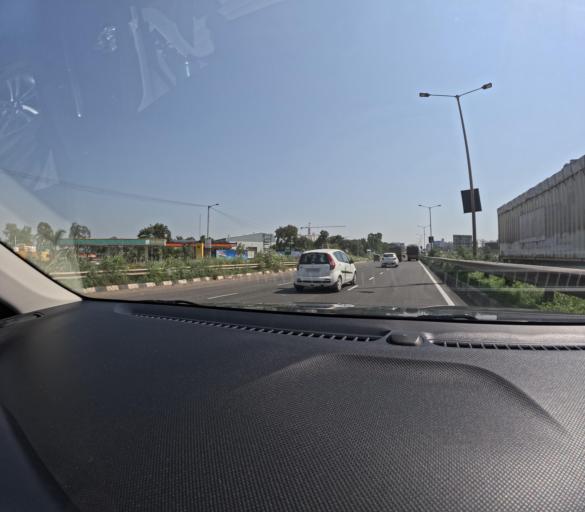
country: IN
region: Maharashtra
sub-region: Pune Division
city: Pimpri
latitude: 18.6306
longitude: 73.7425
